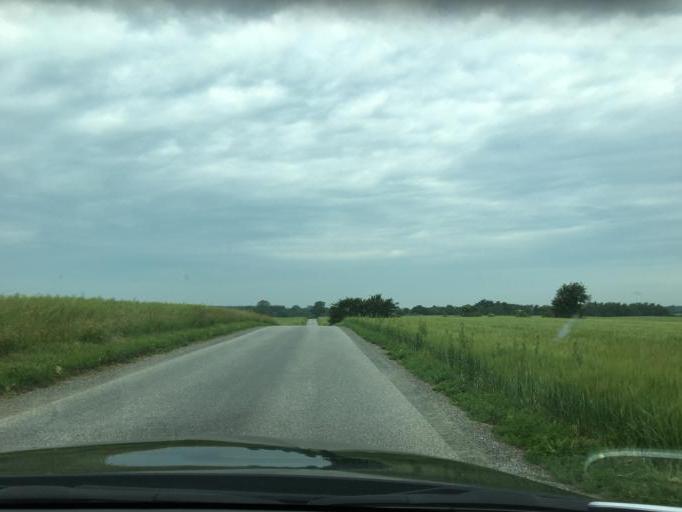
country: DK
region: South Denmark
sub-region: Fredericia Kommune
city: Taulov
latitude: 55.6153
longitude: 9.5571
